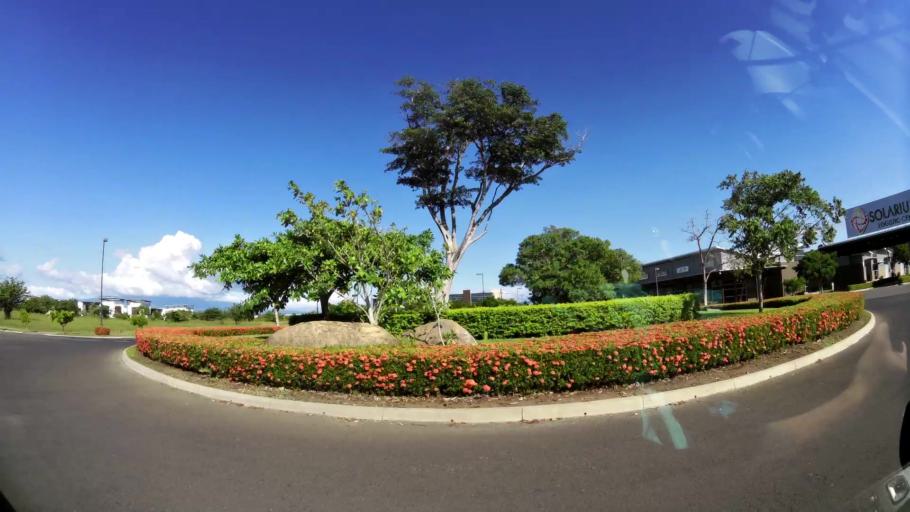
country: CR
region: Guanacaste
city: Liberia
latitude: 10.5910
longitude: -85.5352
